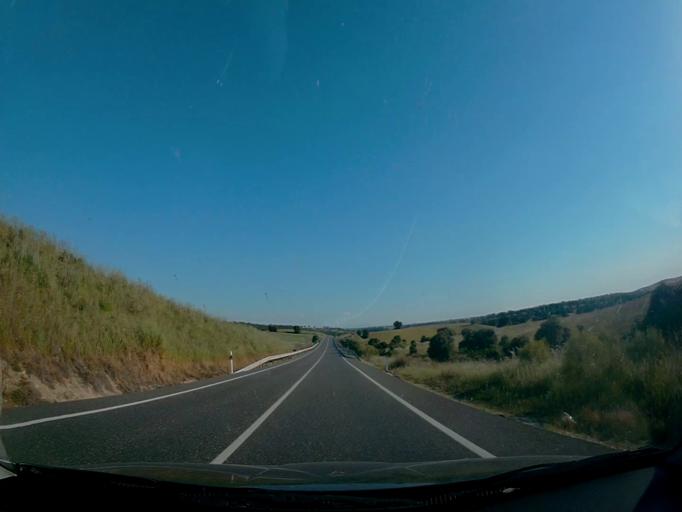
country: ES
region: Castille-La Mancha
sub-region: Province of Toledo
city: Almorox
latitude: 40.2088
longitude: -4.3969
